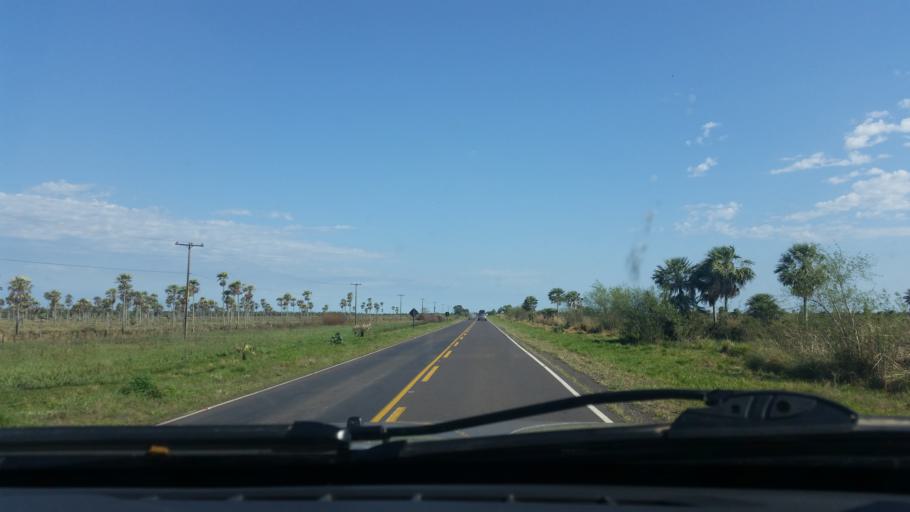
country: PY
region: Presidente Hayes
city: Benjamin Aceval
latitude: -24.6843
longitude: -57.9716
